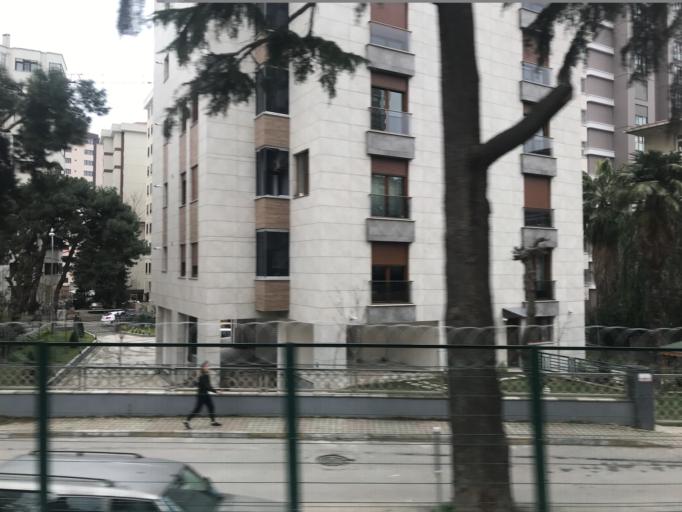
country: TR
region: Istanbul
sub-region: Atasehir
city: Atasehir
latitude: 40.9669
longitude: 29.0787
